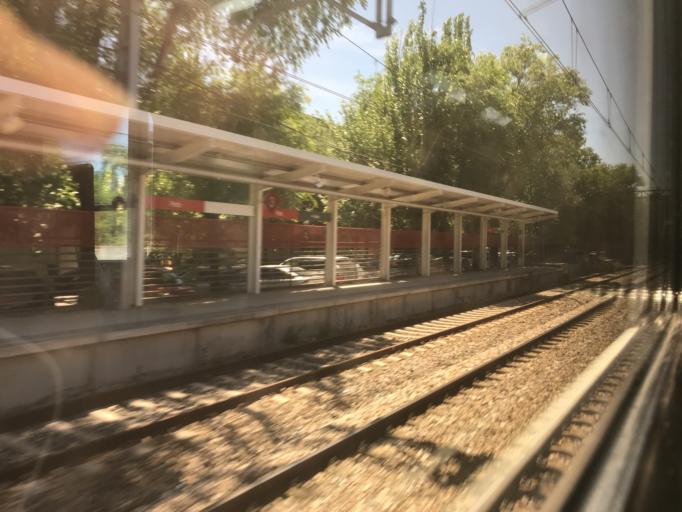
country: ES
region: Madrid
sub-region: Provincia de Madrid
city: Pinto
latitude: 40.2420
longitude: -3.7038
